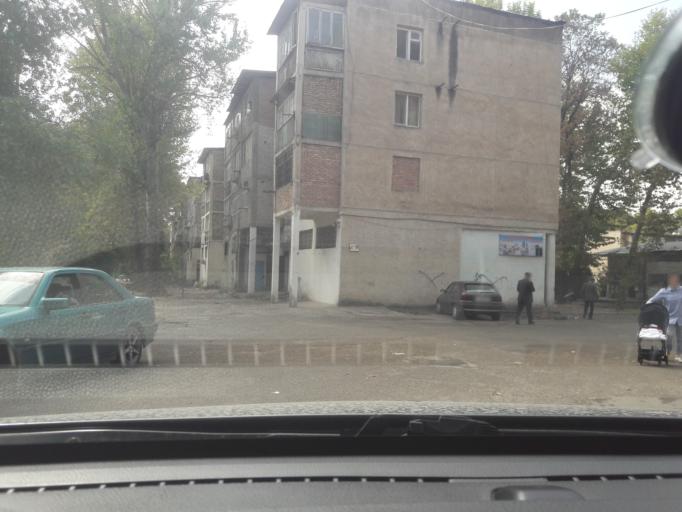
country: TJ
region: Dushanbe
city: Dushanbe
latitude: 38.5873
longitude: 68.7499
